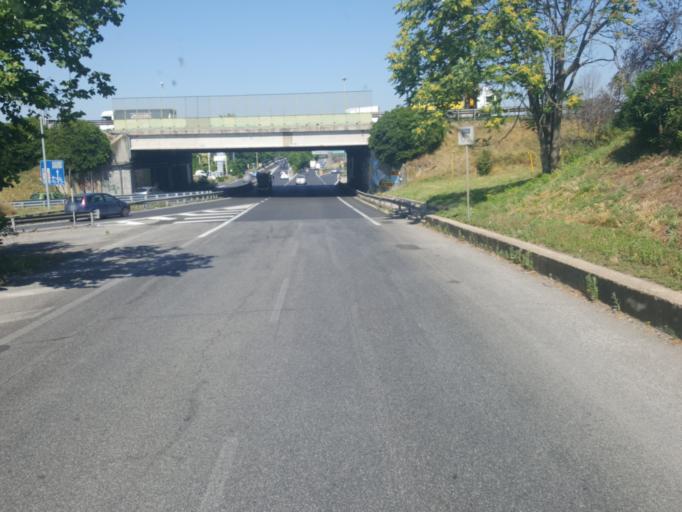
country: IT
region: Latium
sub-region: Citta metropolitana di Roma Capitale
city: Ciampino
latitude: 41.8395
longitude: 12.5928
